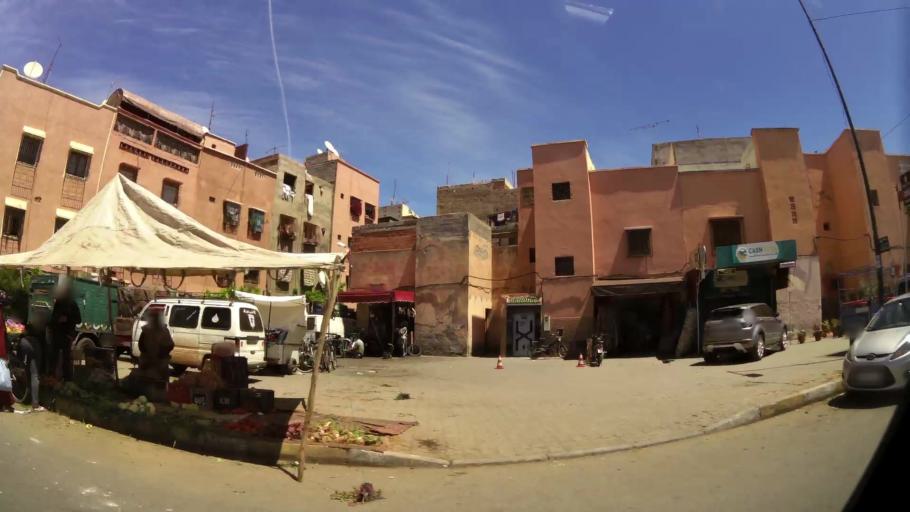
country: MA
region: Marrakech-Tensift-Al Haouz
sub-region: Marrakech
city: Marrakesh
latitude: 31.6539
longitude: -7.9953
